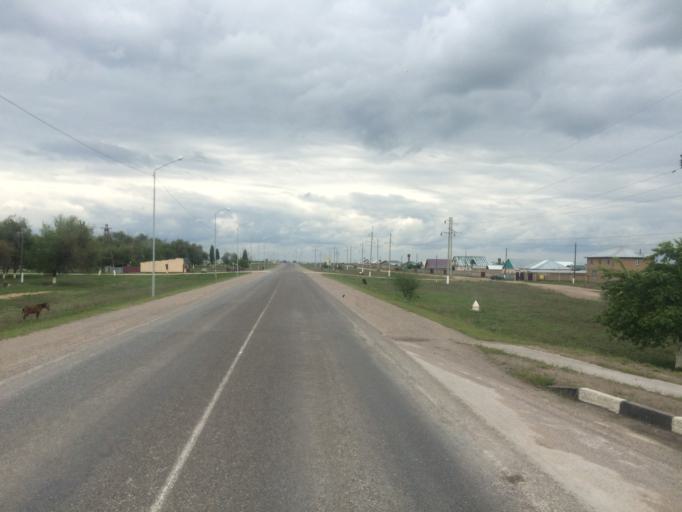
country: KG
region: Chuy
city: Sokuluk
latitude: 43.2488
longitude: 74.2930
